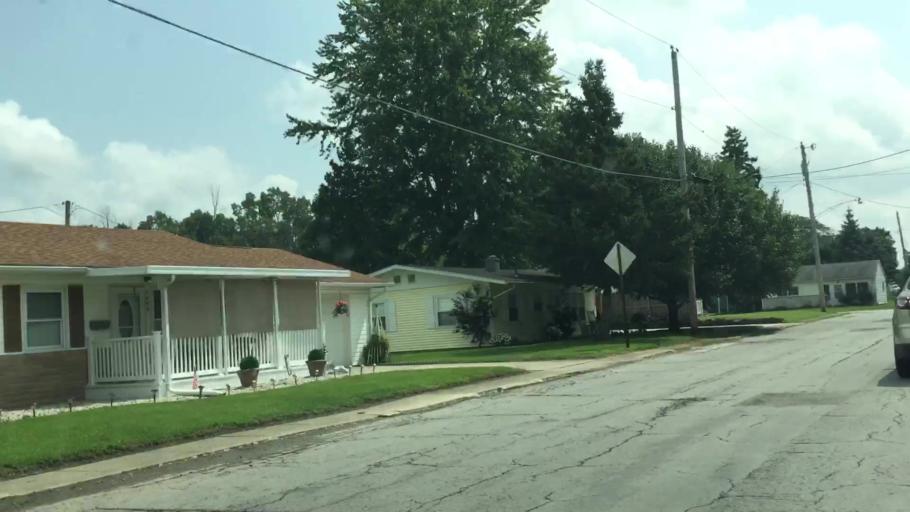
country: US
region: Ohio
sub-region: Logan County
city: Bellefontaine
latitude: 40.3416
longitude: -83.7594
